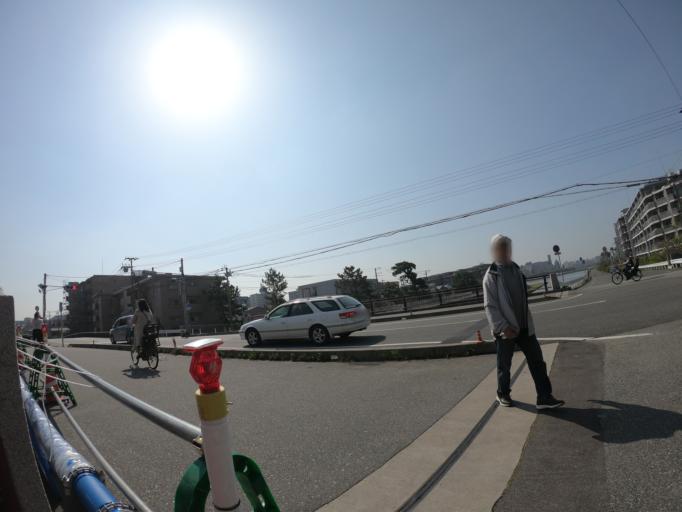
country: JP
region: Hyogo
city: Nishinomiya-hama
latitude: 34.7273
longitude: 135.3288
